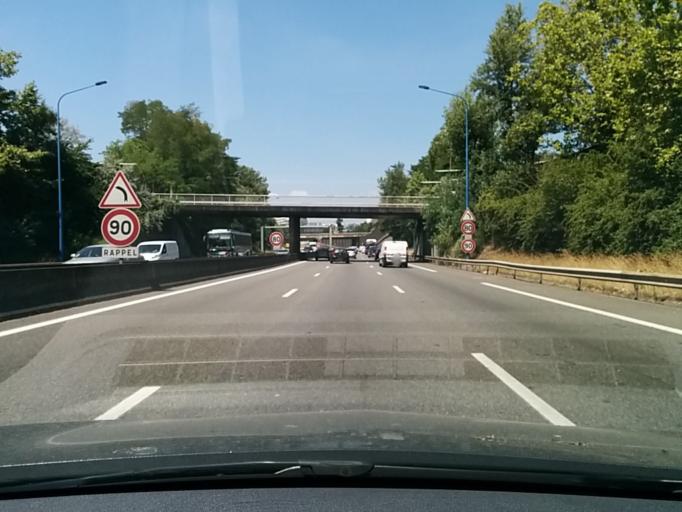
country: FR
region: Midi-Pyrenees
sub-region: Departement de la Haute-Garonne
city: Toulouse
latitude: 43.5749
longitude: 1.4468
